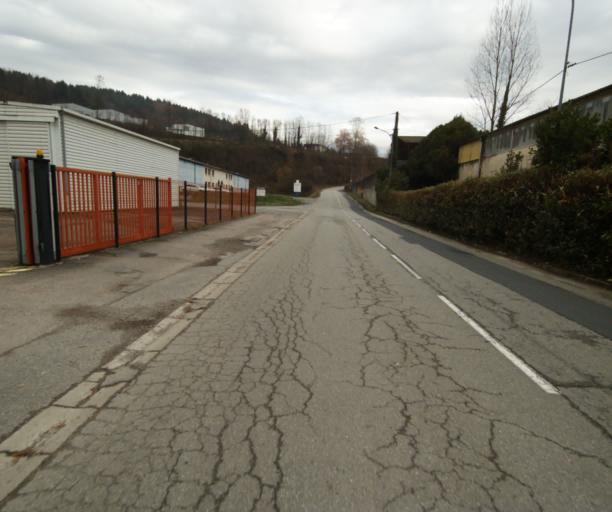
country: FR
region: Limousin
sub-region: Departement de la Correze
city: Chameyrat
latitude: 45.2402
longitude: 1.7348
